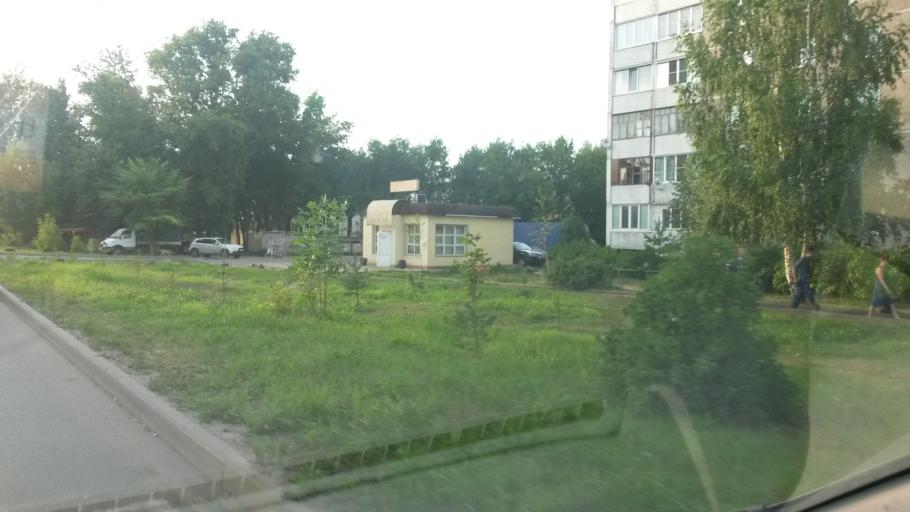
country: RU
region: Ivanovo
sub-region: Gorod Ivanovo
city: Ivanovo
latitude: 57.0111
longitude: 40.9390
